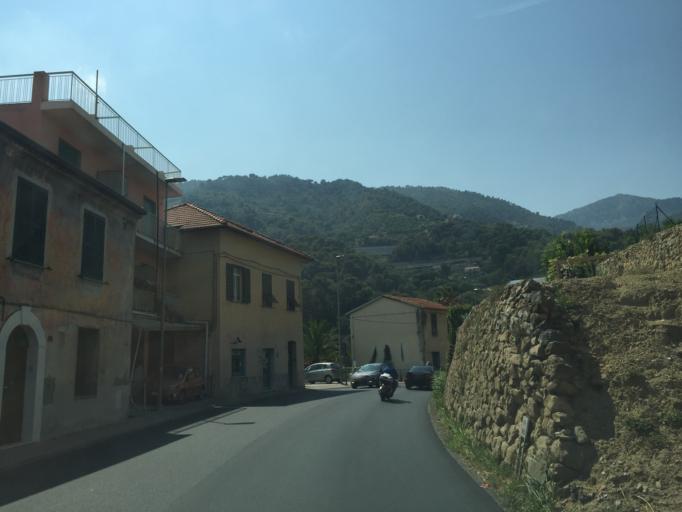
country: IT
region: Liguria
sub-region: Provincia di Imperia
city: Ventimiglia
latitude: 43.7936
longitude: 7.5660
